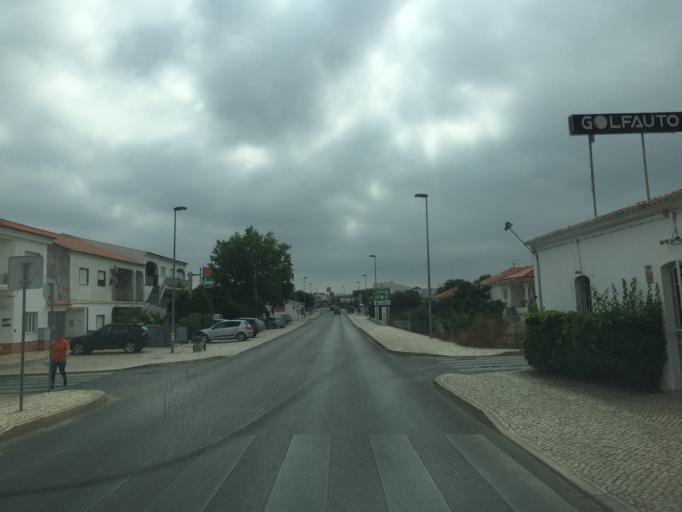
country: PT
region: Faro
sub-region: Loule
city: Almancil
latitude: 37.0849
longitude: -8.0252
